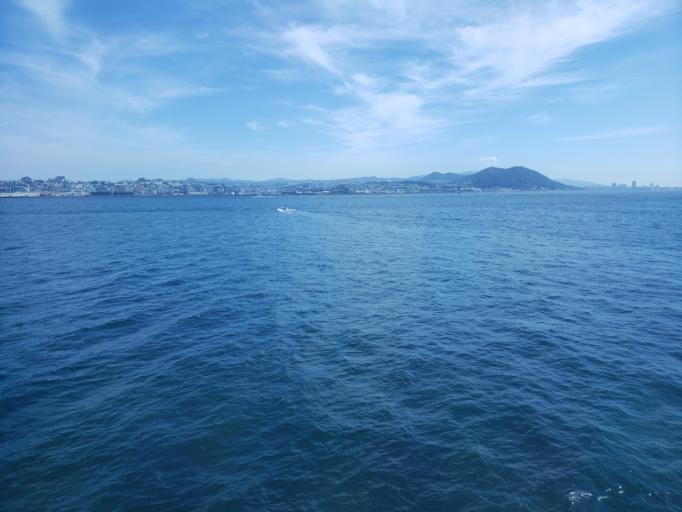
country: JP
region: Hyogo
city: Akashi
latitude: 34.6058
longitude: 135.0477
